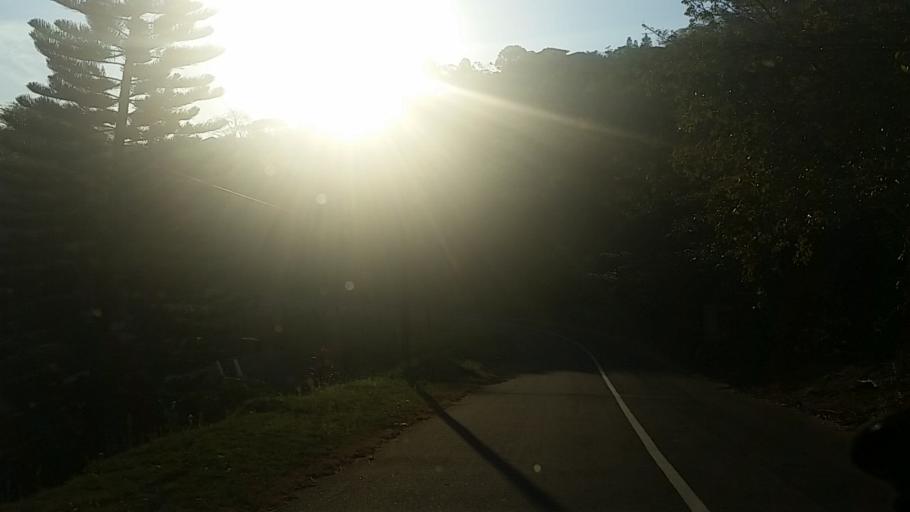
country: ZA
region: KwaZulu-Natal
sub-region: eThekwini Metropolitan Municipality
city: Berea
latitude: -29.8512
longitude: 30.9212
